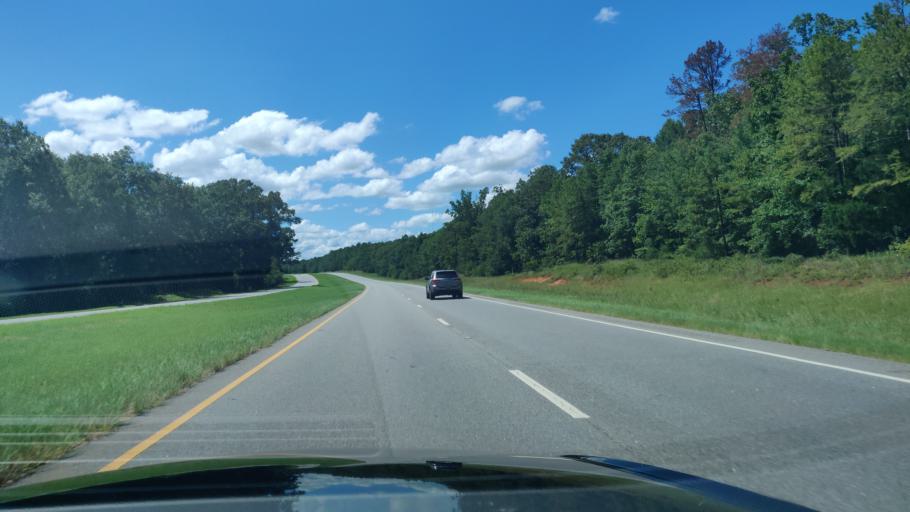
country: US
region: Georgia
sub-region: Webster County
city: Preston
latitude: 31.9097
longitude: -84.5301
